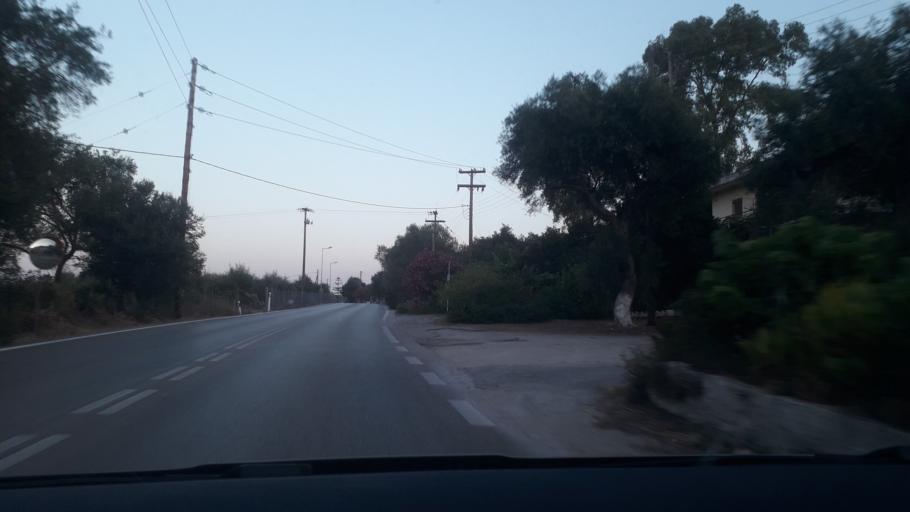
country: GR
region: Ionian Islands
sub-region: Nomos Kerkyras
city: Perivoli
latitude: 39.4432
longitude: 19.9473
